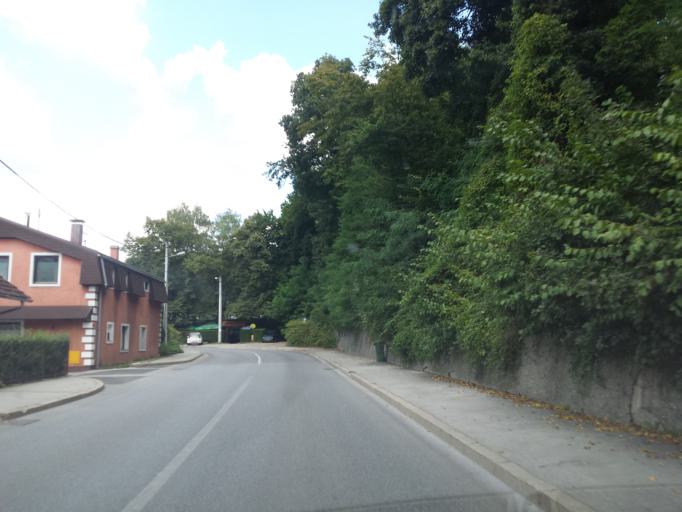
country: HR
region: Grad Zagreb
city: Zagreb
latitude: 45.8277
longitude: 16.0136
